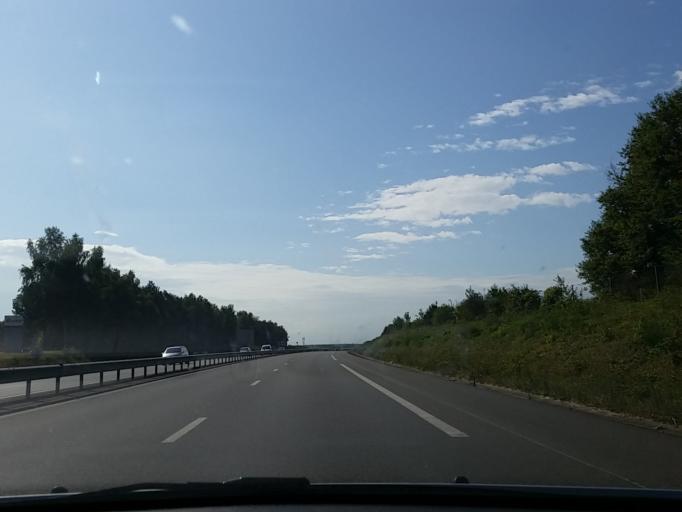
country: FR
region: Centre
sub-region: Departement du Cher
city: Trouy
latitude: 47.0274
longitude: 2.3777
